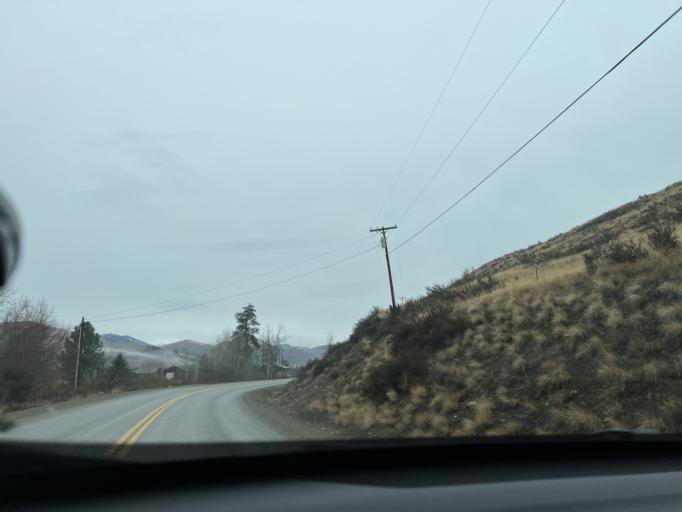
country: US
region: Washington
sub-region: Okanogan County
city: Brewster
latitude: 48.4894
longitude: -120.1790
